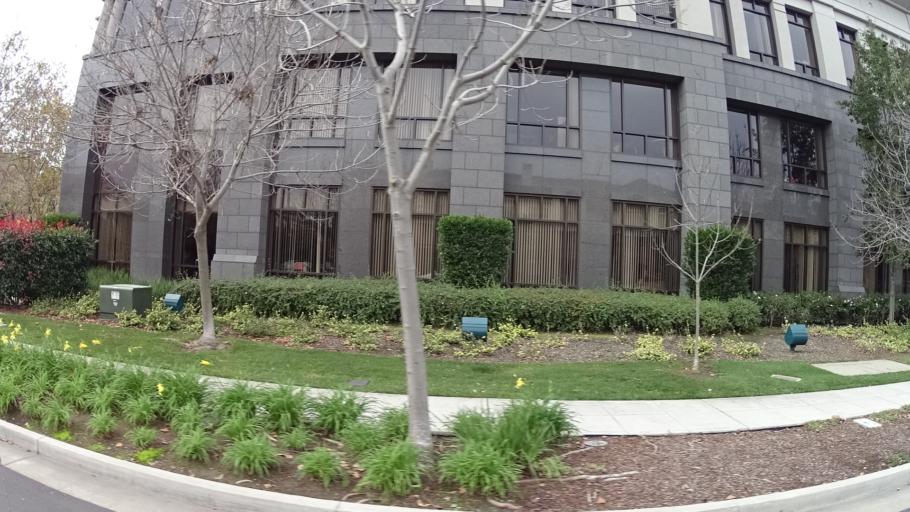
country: US
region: California
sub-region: San Mateo County
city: Foster City
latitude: 37.5446
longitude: -122.2932
